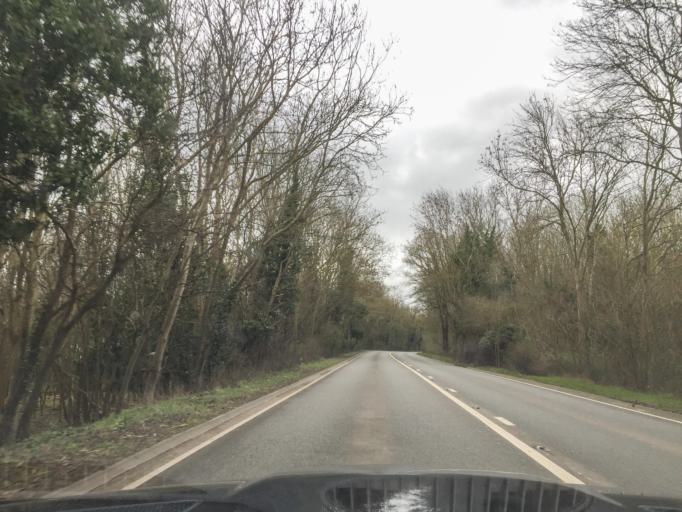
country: GB
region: England
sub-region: Warwickshire
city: Wellesbourne Mountford
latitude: 52.1825
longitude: -1.5978
